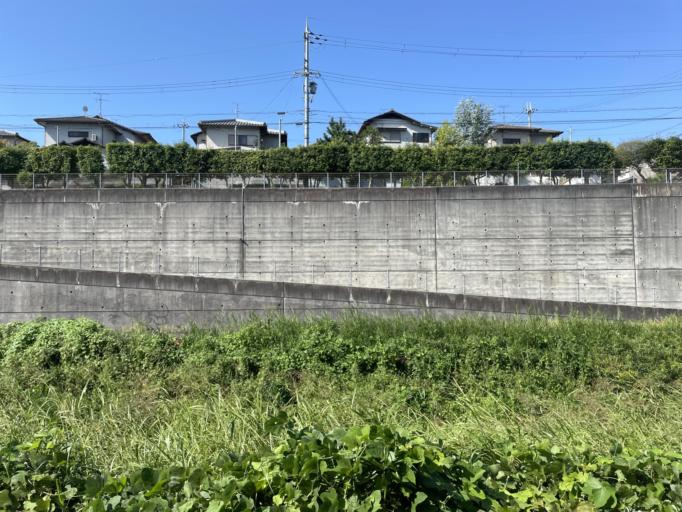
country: JP
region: Nara
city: Kashihara-shi
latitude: 34.4696
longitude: 135.7980
